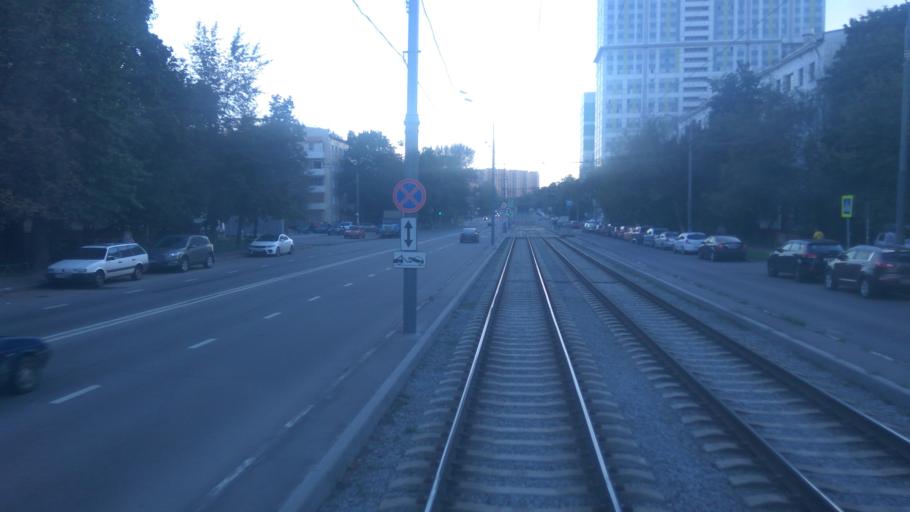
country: RU
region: Moskovskaya
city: Bogorodskoye
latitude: 55.8114
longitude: 37.7322
